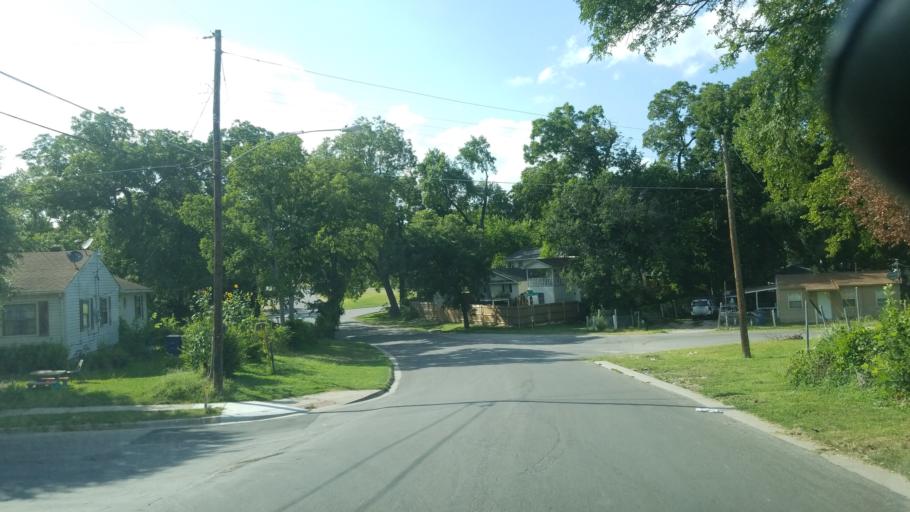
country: US
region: Texas
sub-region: Dallas County
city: Balch Springs
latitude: 32.7702
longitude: -96.7088
